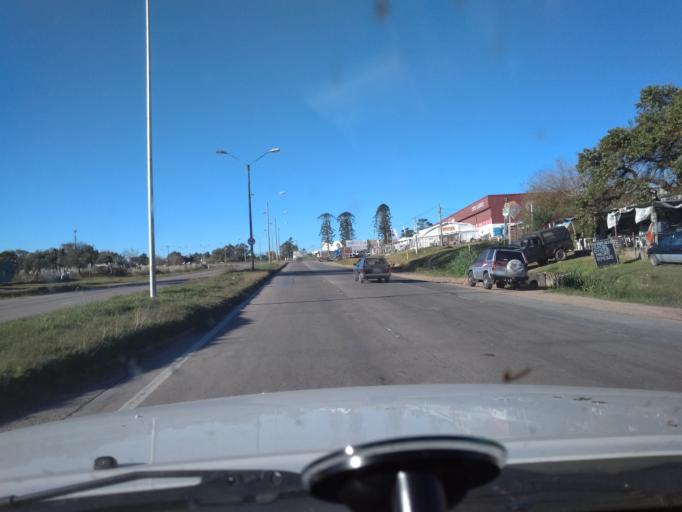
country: UY
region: Canelones
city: Joaquin Suarez
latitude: -34.7728
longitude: -56.0293
